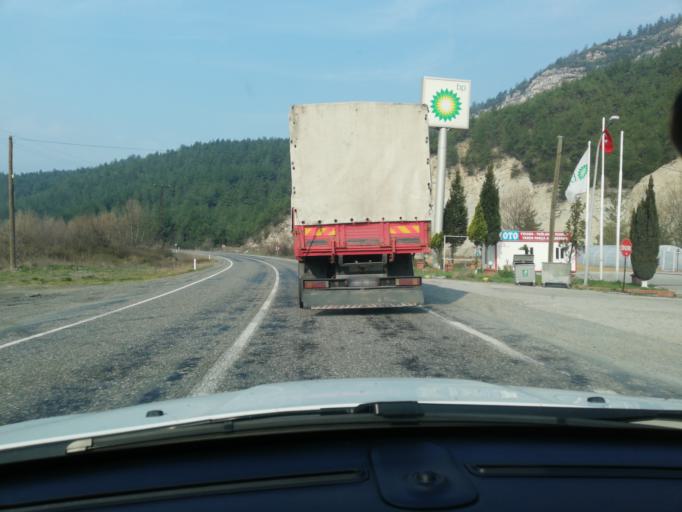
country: TR
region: Karabuk
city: Karabuk
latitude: 41.1666
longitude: 32.5724
